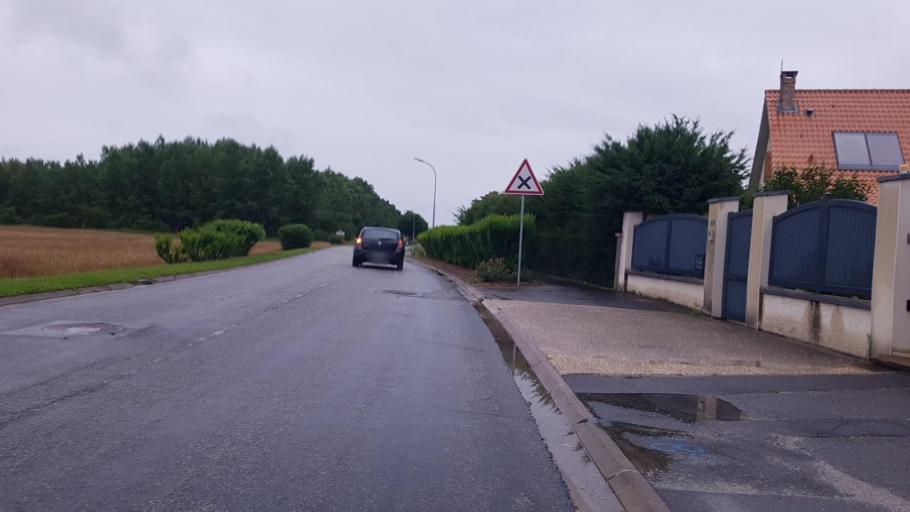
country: FR
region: Champagne-Ardenne
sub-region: Departement de la Marne
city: Sarry
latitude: 48.9099
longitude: 4.4248
